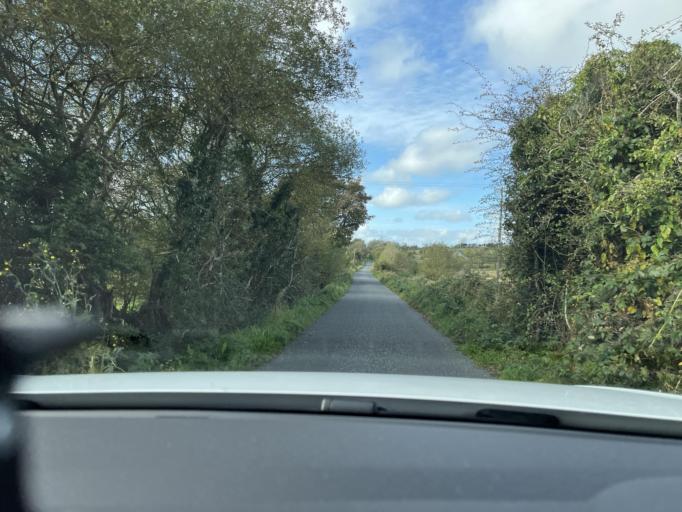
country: IE
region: Connaught
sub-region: Sligo
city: Ballymote
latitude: 54.0748
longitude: -8.4362
